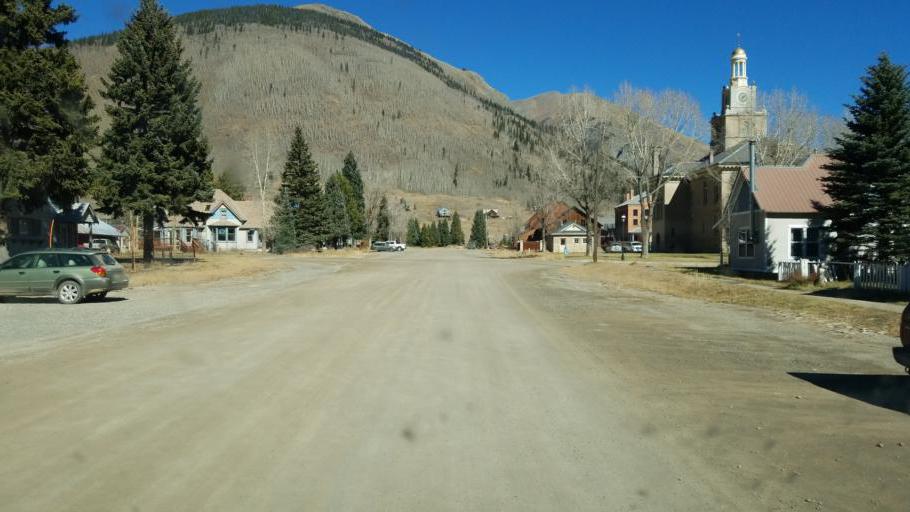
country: US
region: Colorado
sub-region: San Juan County
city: Silverton
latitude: 37.8143
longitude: -107.6633
